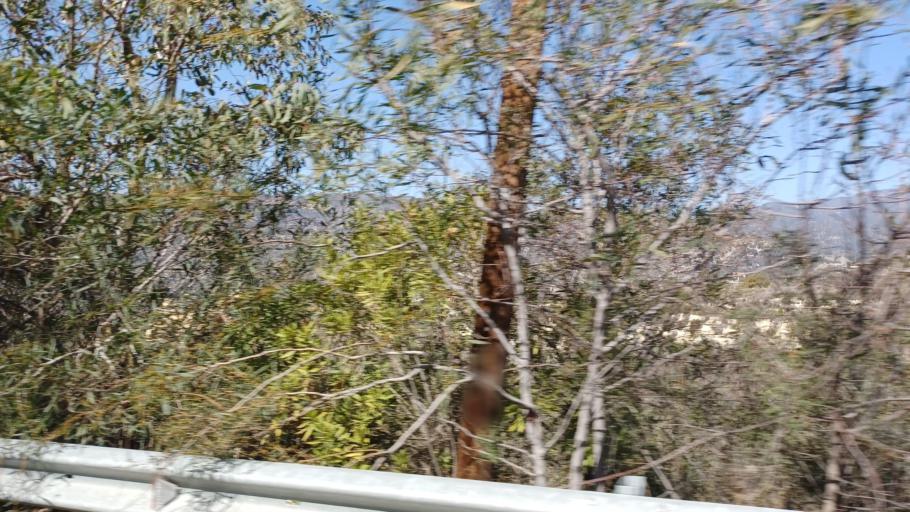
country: CY
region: Limassol
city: Pelendri
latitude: 34.8215
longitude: 32.9168
